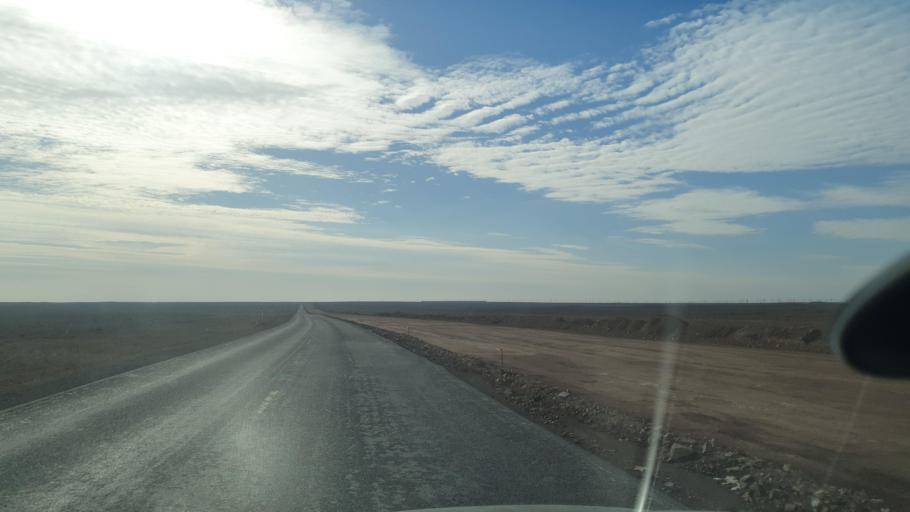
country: KZ
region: Qaraghandy
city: Saryshaghan
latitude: 45.9673
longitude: 73.5467
